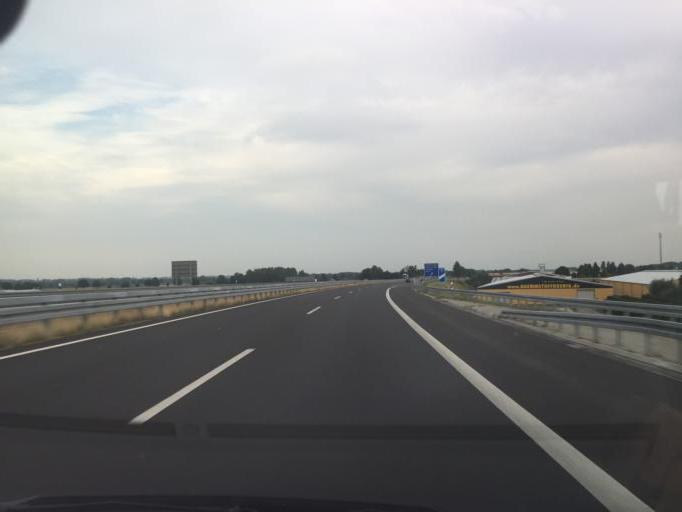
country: NL
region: Limburg
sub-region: Gemeente Venlo
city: Venlo
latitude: 51.3333
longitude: 6.2040
